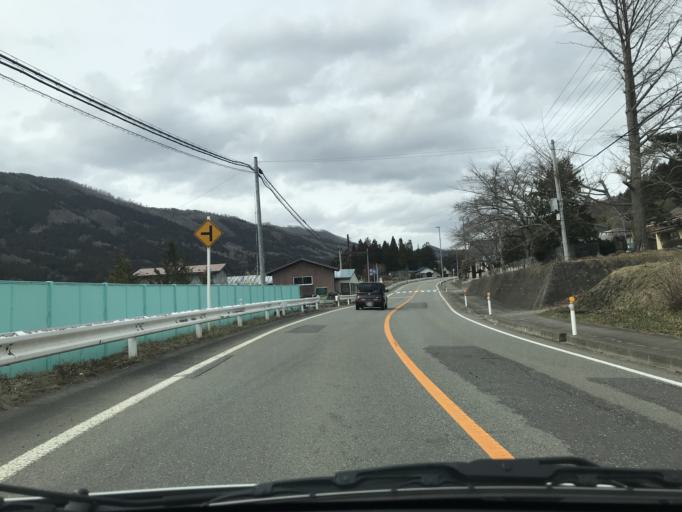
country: JP
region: Iwate
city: Tono
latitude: 39.3309
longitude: 141.4532
